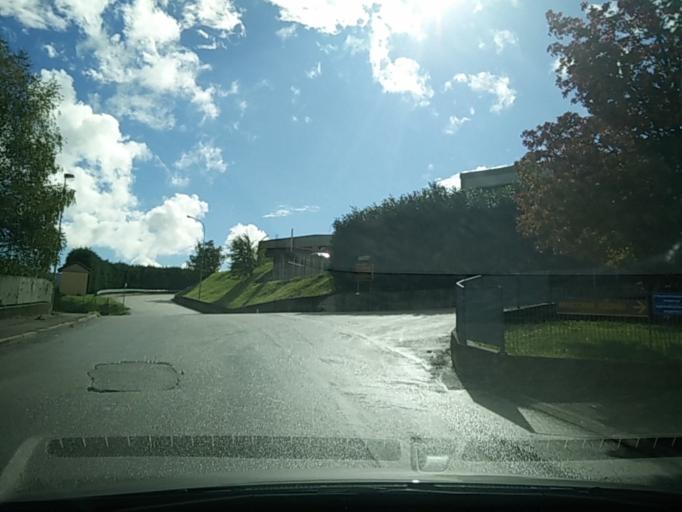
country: IT
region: Veneto
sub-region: Provincia di Belluno
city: Quero
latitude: 45.9254
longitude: 11.9367
